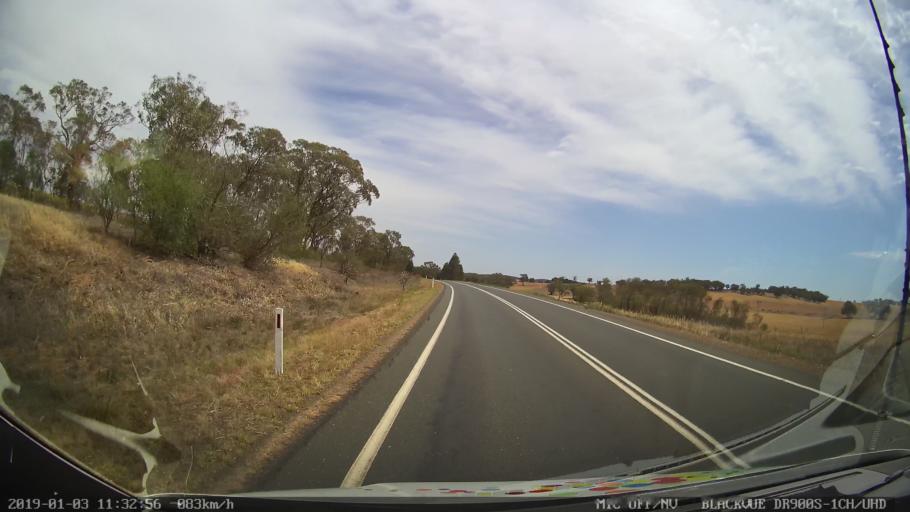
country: AU
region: New South Wales
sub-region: Weddin
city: Grenfell
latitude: -33.9523
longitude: 148.1758
